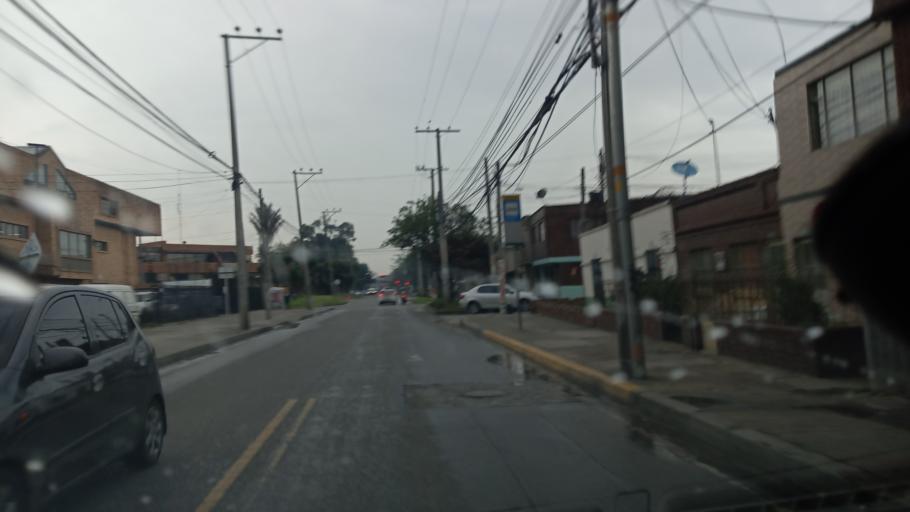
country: CO
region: Bogota D.C.
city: Bogota
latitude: 4.6812
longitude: -74.1291
